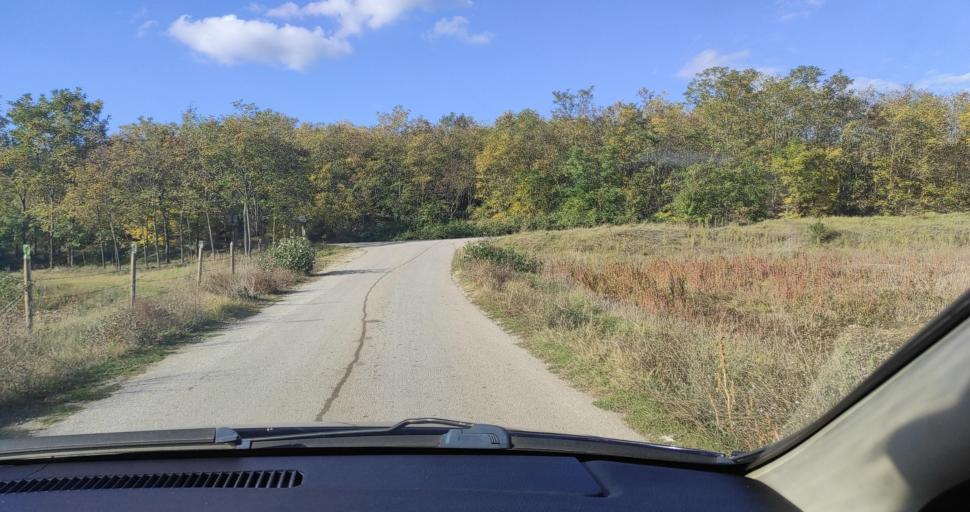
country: MK
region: Prilep
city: Topolcani
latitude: 41.2844
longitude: 21.4202
